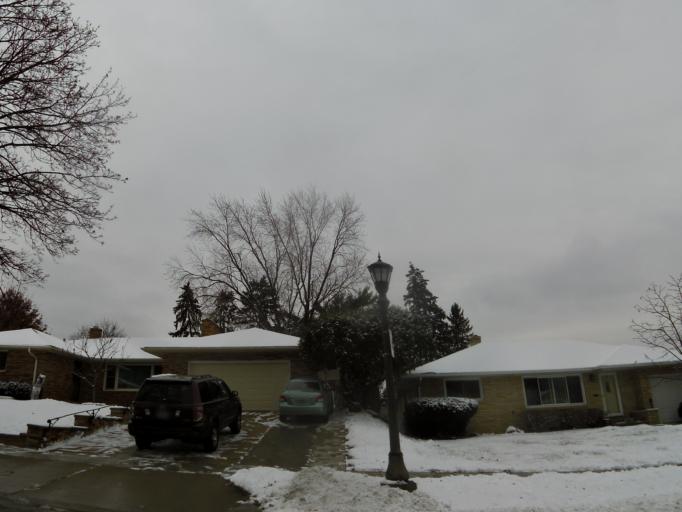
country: US
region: Minnesota
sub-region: Ramsey County
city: Maplewood
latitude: 44.9568
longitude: -93.0388
